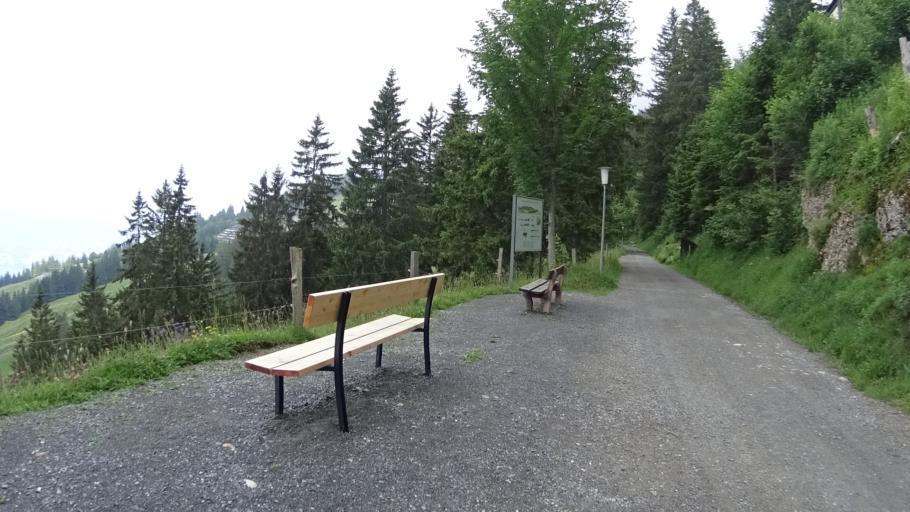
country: CH
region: Lucerne
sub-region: Lucerne-Land District
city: Vitznau
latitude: 47.0428
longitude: 8.4742
